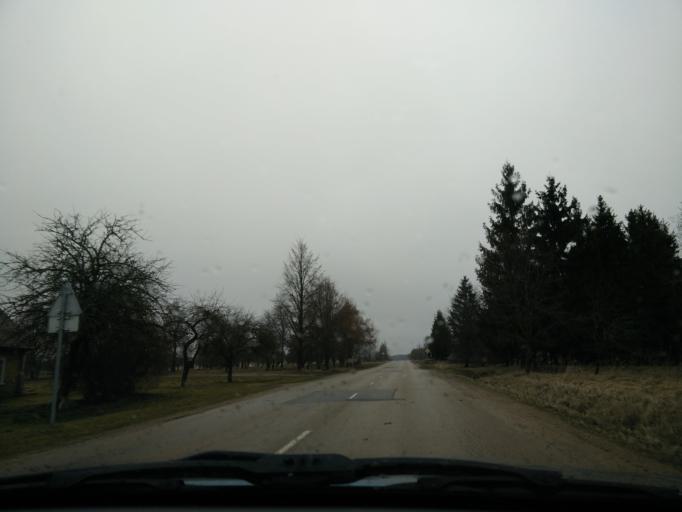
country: LT
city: Ariogala
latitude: 55.3889
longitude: 23.3423
